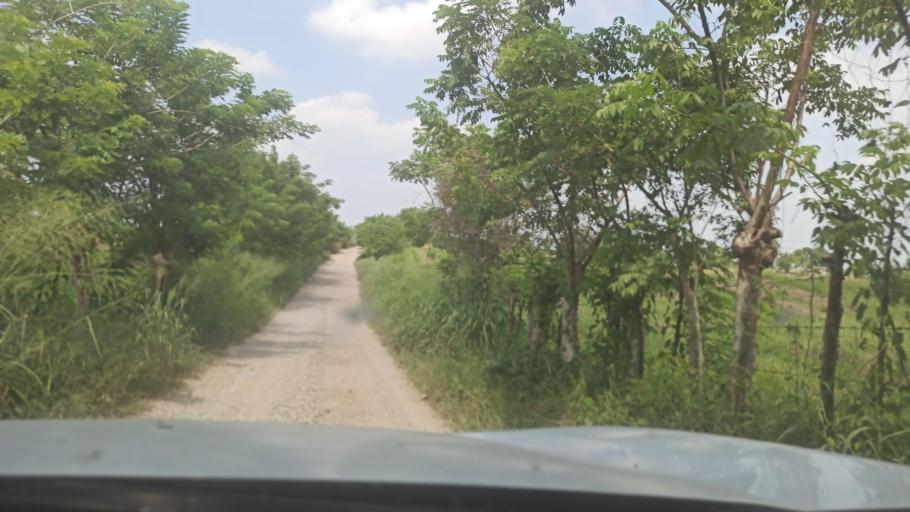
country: MX
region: Veracruz
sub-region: Atzalan
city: Colonias Pedernales
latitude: 20.0417
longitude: -97.0054
